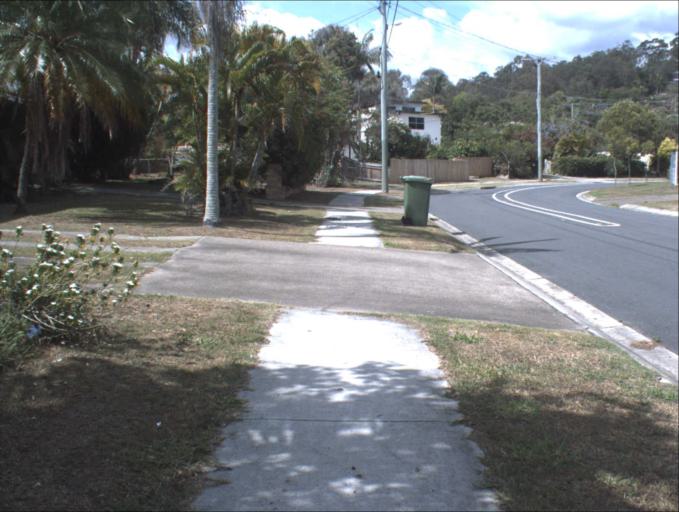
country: AU
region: Queensland
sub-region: Logan
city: Beenleigh
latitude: -27.7183
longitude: 153.1909
